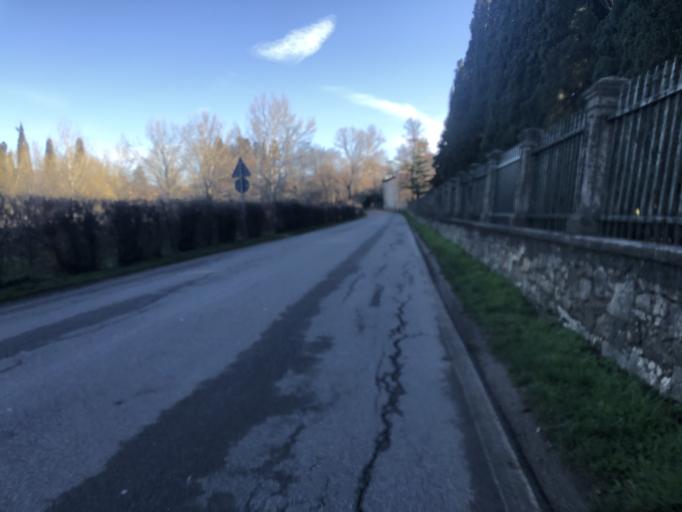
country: IT
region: Veneto
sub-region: Provincia di Verona
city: San Pietro in Cariano
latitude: 45.5078
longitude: 10.8850
